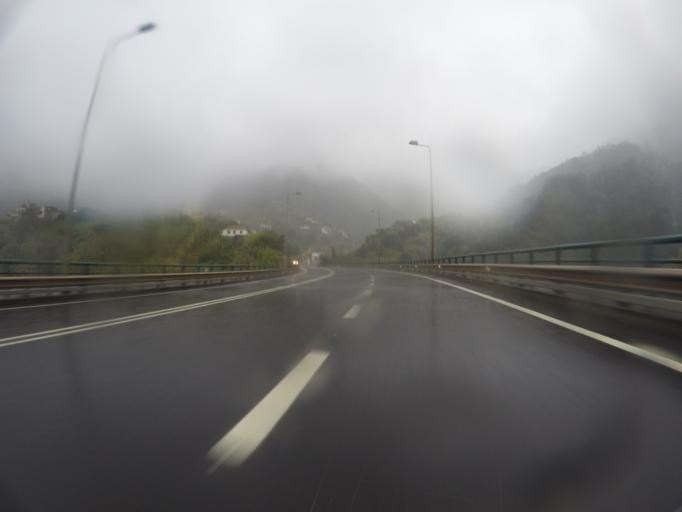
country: PT
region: Madeira
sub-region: Santa Cruz
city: Santa Cruz
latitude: 32.7559
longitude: -16.8215
